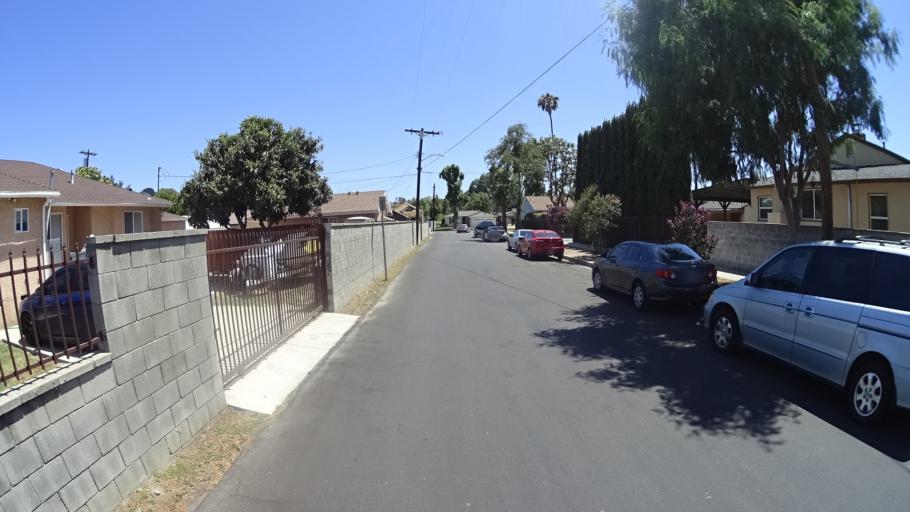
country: US
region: California
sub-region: Los Angeles County
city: Northridge
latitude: 34.1937
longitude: -118.5246
